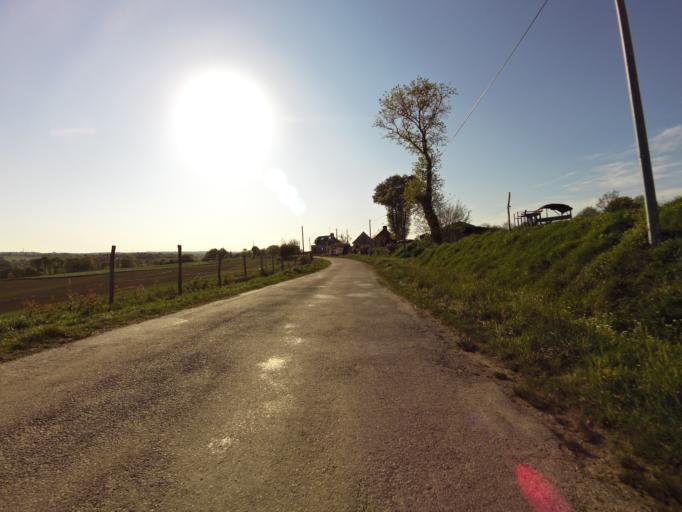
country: FR
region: Brittany
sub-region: Departement du Morbihan
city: Molac
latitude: 47.7323
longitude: -2.4716
